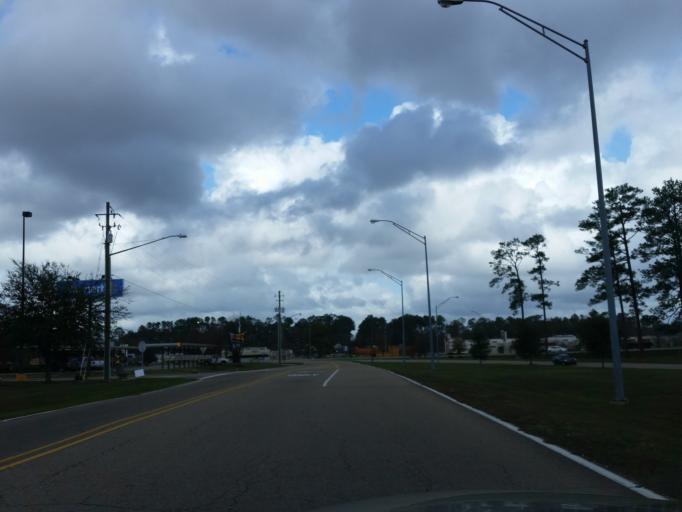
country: US
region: Mississippi
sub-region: Forrest County
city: Hattiesburg
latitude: 31.3072
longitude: -89.3185
